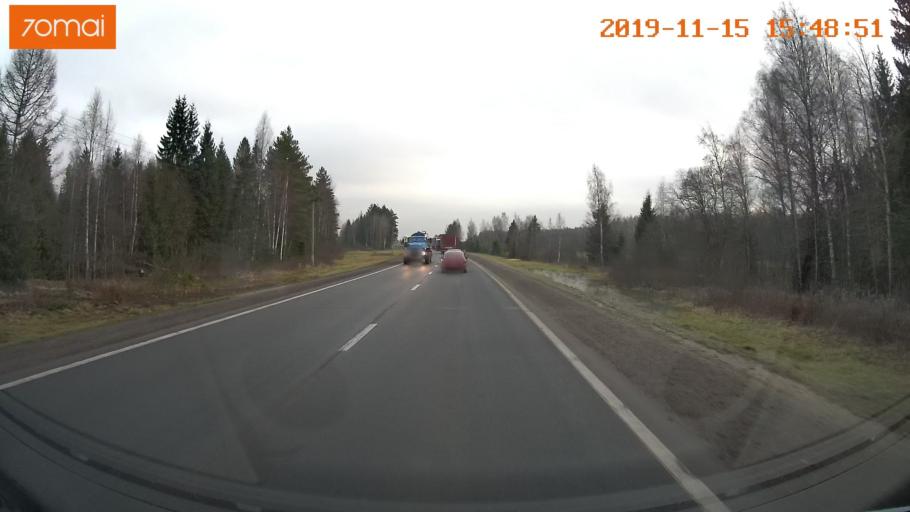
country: RU
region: Jaroslavl
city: Danilov
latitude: 57.9225
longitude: 40.0066
